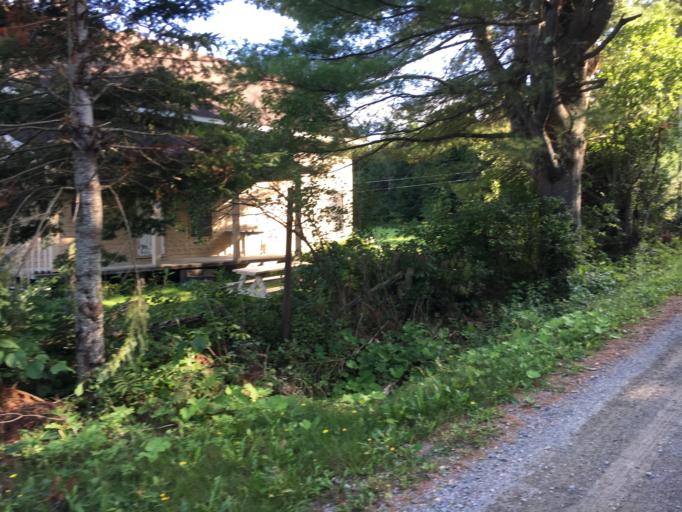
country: CA
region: Quebec
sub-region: Chaudiere-Appalaches
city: Saint-Joseph-de-Coleraine
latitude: 45.6665
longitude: -71.3985
